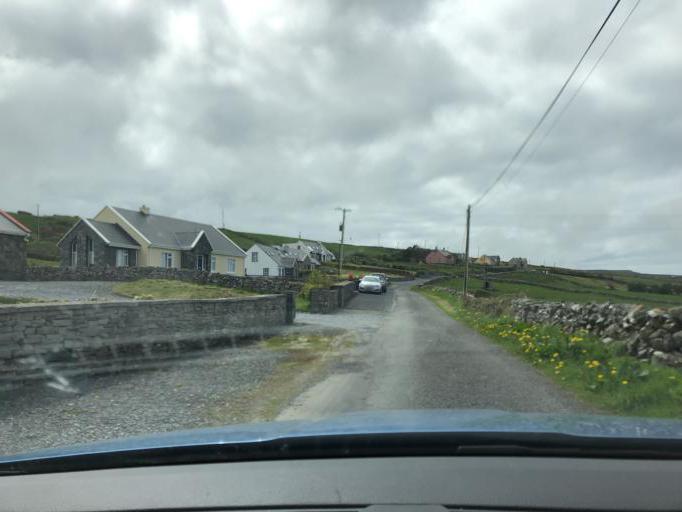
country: IE
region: Connaught
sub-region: County Galway
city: Bearna
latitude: 52.9979
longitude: -9.3994
